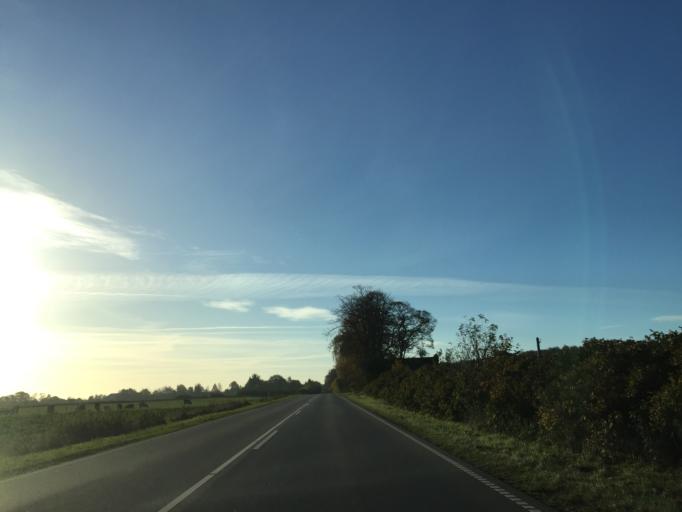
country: DK
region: Central Jutland
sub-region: Skanderborg Kommune
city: Galten
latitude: 56.1029
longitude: 9.8943
